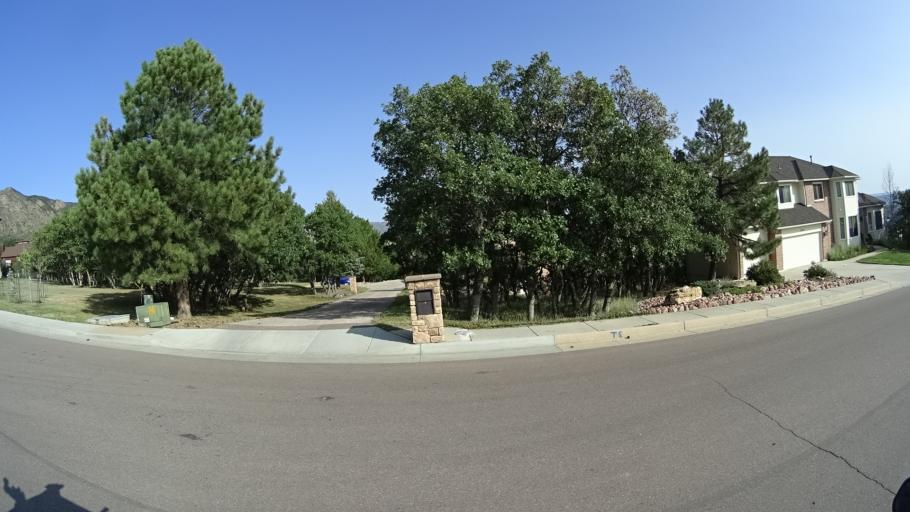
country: US
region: Colorado
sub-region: El Paso County
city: Colorado Springs
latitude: 38.8220
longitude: -104.8750
